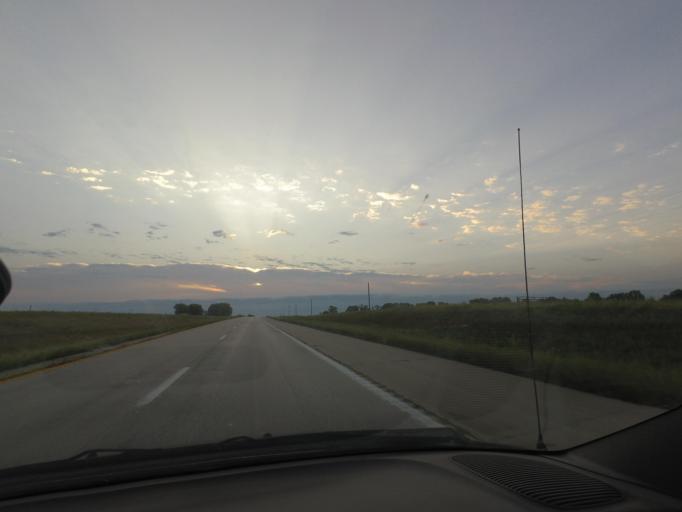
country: US
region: Missouri
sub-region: Macon County
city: Macon
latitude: 39.7503
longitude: -92.3637
